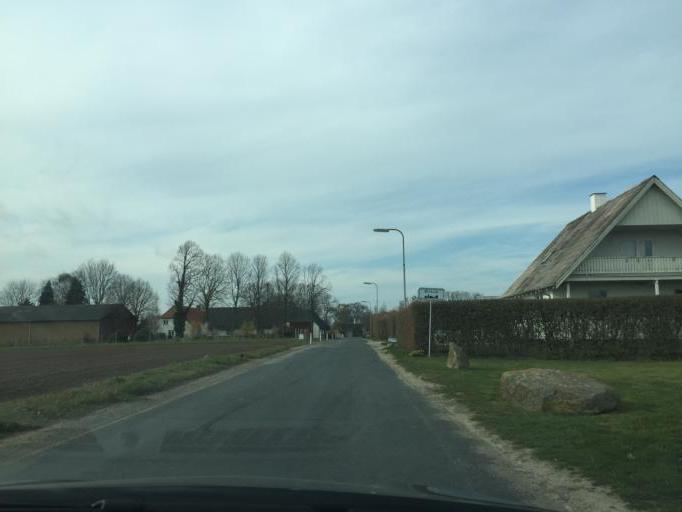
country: DK
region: South Denmark
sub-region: Faaborg-Midtfyn Kommune
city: Arslev
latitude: 55.3325
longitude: 10.5118
